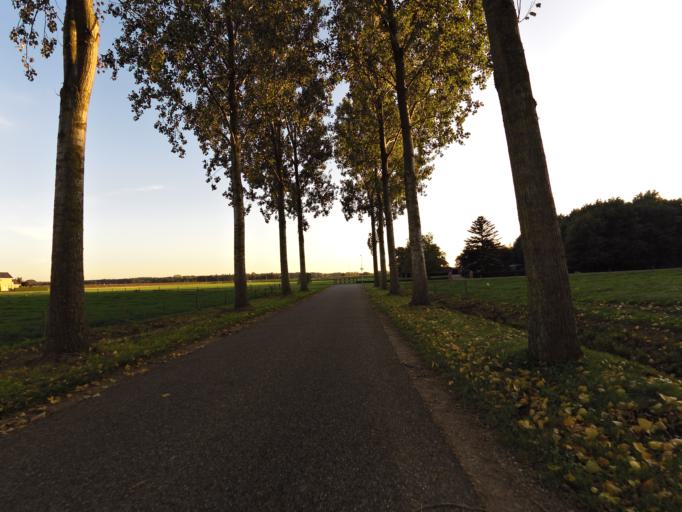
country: NL
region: Gelderland
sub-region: Gemeente Zevenaar
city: Zevenaar
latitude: 51.9233
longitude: 6.1590
